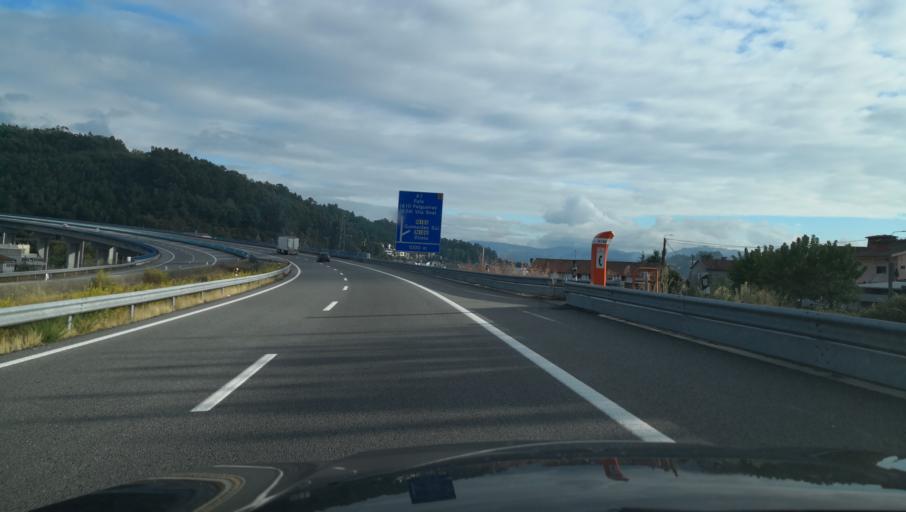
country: PT
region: Braga
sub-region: Guimaraes
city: Candoso
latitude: 41.4116
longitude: -8.3240
